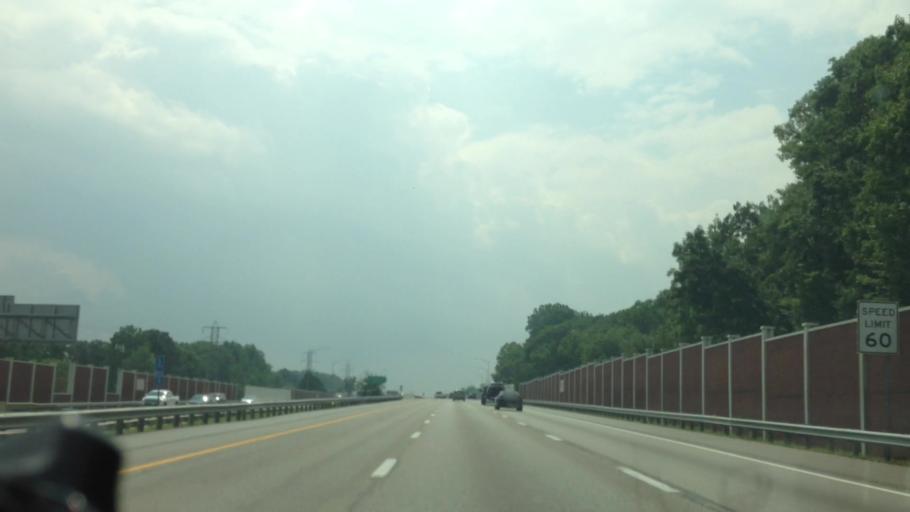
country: US
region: Ohio
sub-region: Cuyahoga County
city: Independence
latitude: 41.3530
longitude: -81.6497
